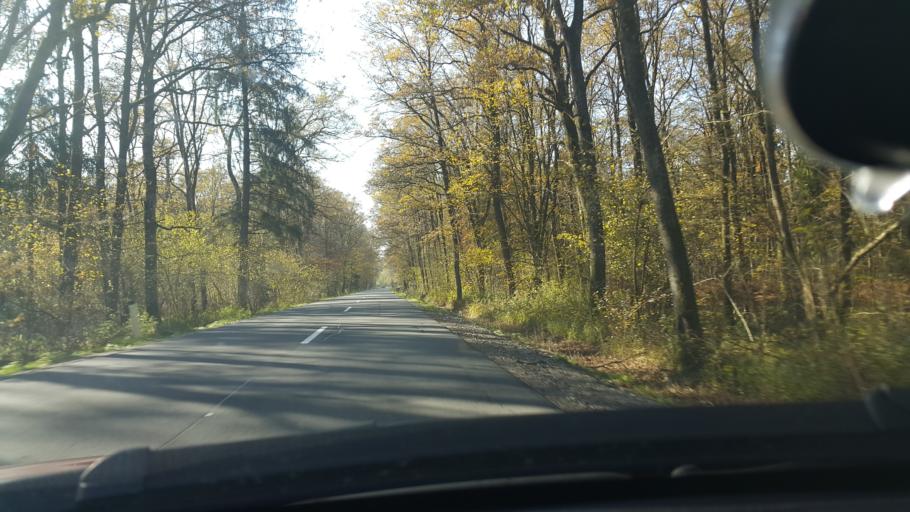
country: SI
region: Brezice
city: Brezice
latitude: 45.9390
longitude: 15.6506
